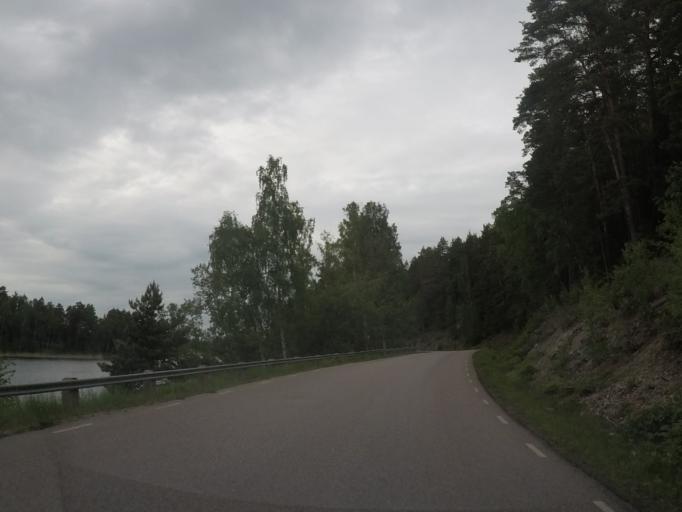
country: SE
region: Soedermanland
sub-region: Nykopings Kommun
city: Stigtomta
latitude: 58.9405
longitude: 16.8904
